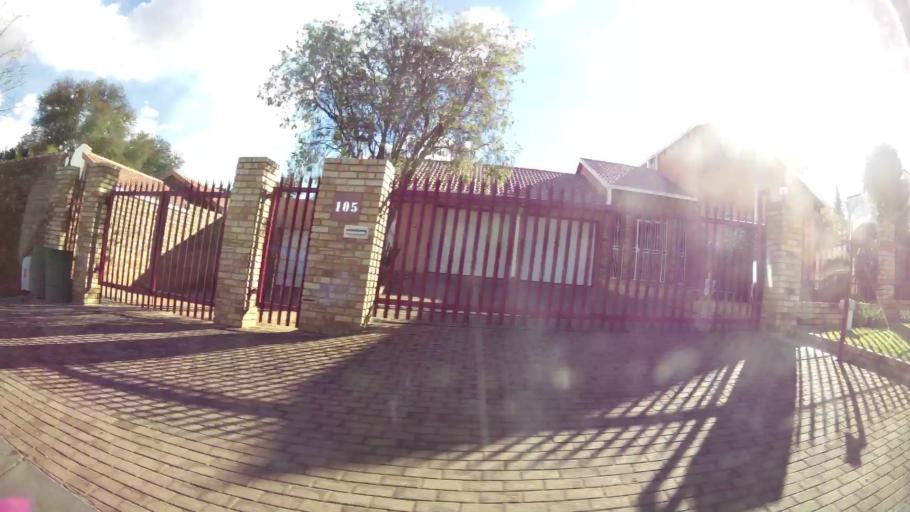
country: ZA
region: North-West
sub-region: Dr Kenneth Kaunda District Municipality
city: Klerksdorp
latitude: -26.8236
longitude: 26.6782
